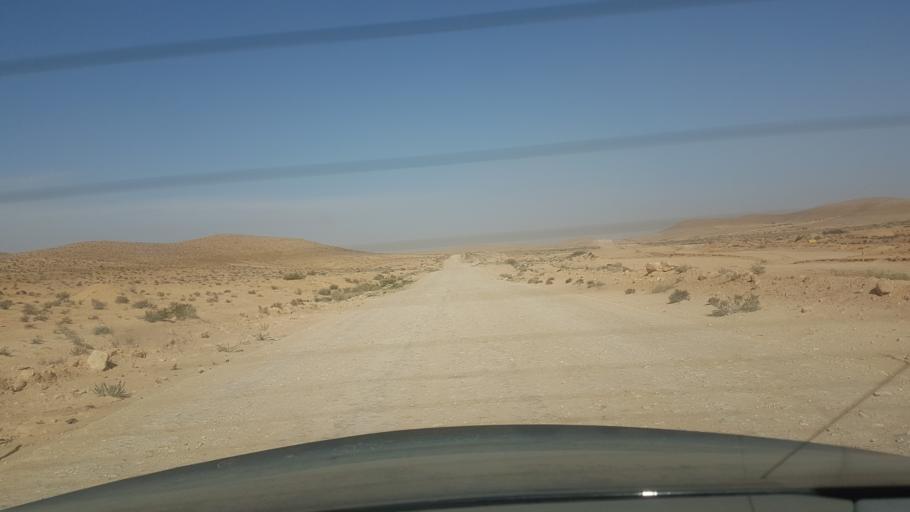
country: TN
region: Qabis
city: Matmata
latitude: 33.6410
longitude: 9.7370
